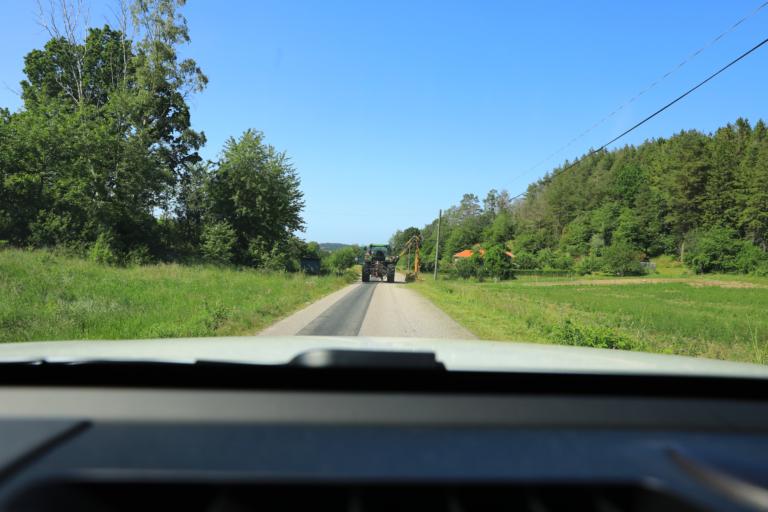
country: SE
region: Halland
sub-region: Varbergs Kommun
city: Veddige
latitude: 57.1925
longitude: 12.3235
